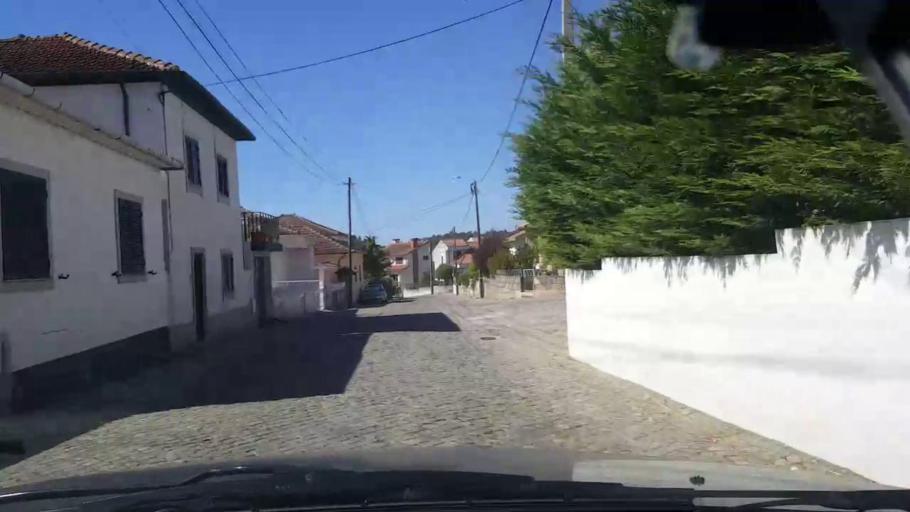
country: PT
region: Porto
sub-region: Maia
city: Gemunde
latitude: 41.2964
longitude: -8.6827
